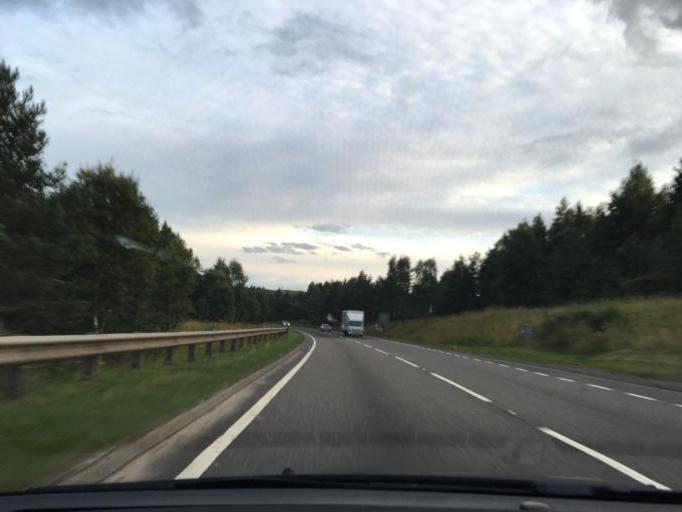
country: GB
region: Scotland
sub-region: Highland
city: Aviemore
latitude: 57.3518
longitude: -4.0062
